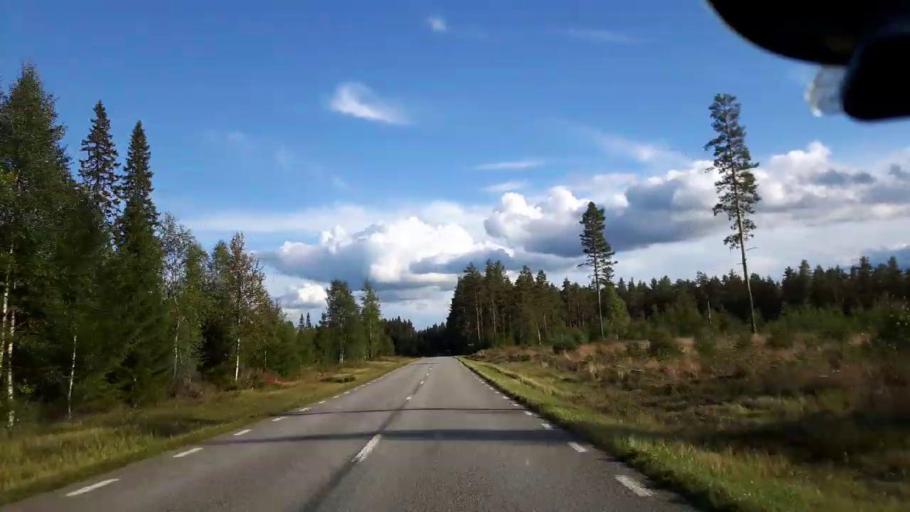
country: SE
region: Jaemtland
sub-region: Stroemsunds Kommun
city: Stroemsund
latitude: 63.4006
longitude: 15.5743
